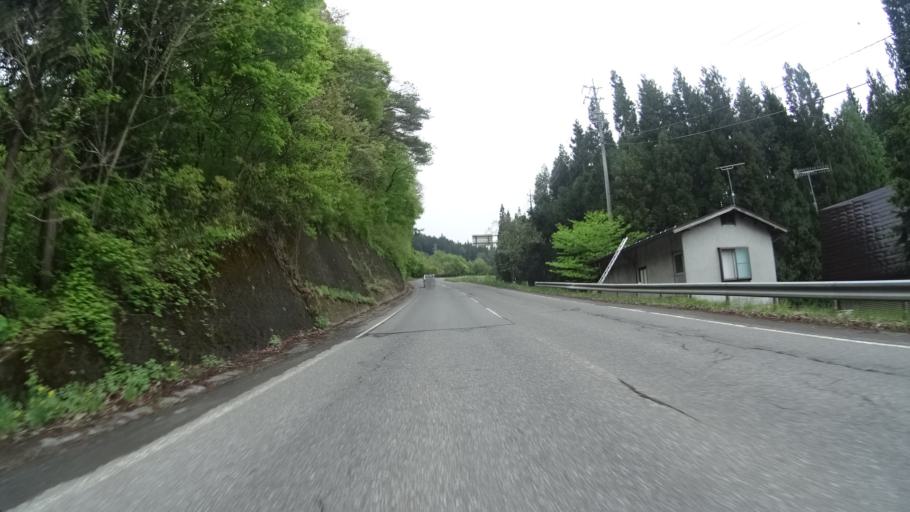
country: JP
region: Nagano
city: Nakano
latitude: 36.7231
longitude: 138.4455
